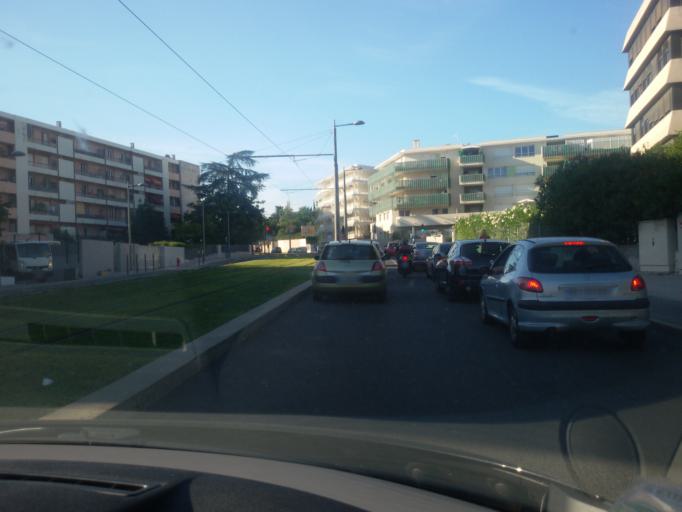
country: FR
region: Languedoc-Roussillon
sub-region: Departement de l'Herault
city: Montpellier
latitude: 43.5934
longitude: 3.8795
